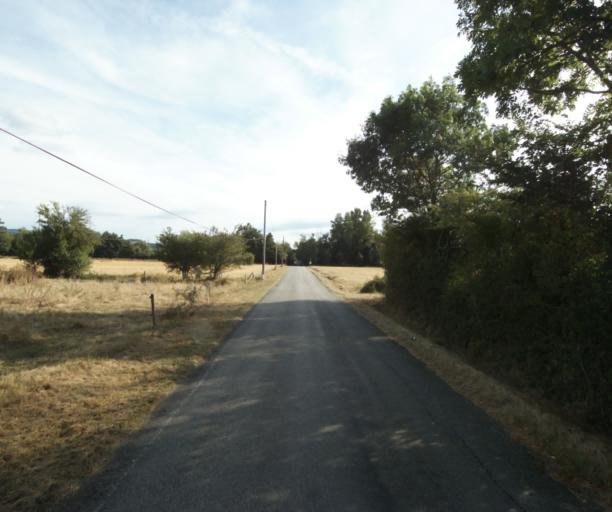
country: FR
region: Midi-Pyrenees
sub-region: Departement de la Haute-Garonne
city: Revel
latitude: 43.4736
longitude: 1.9985
